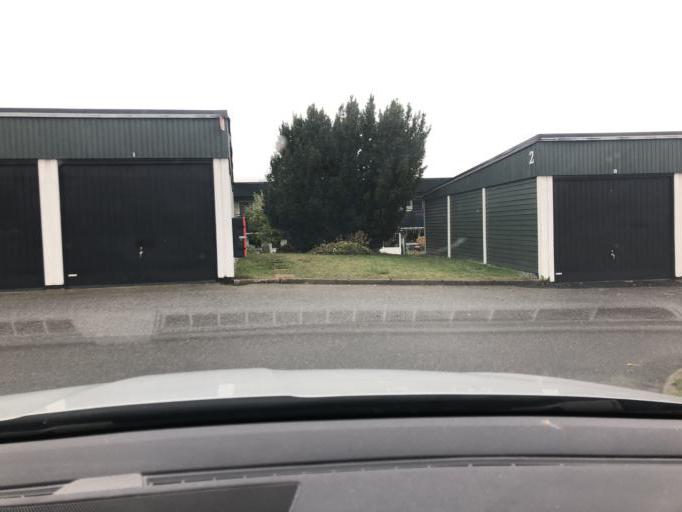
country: SE
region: Stockholm
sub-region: Botkyrka Kommun
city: Alby
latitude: 59.2356
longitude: 17.8622
